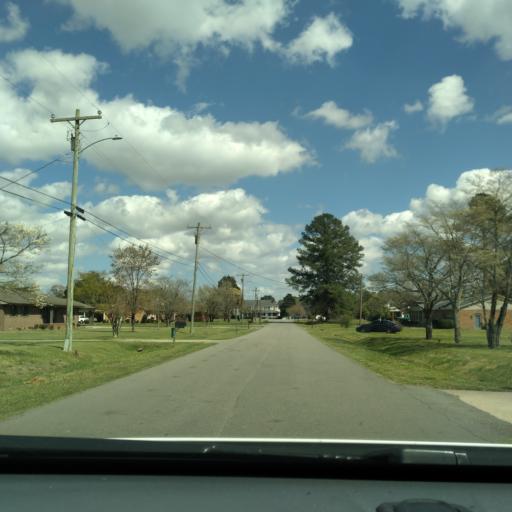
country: US
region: North Carolina
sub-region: Washington County
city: Plymouth
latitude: 35.8519
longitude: -76.7333
